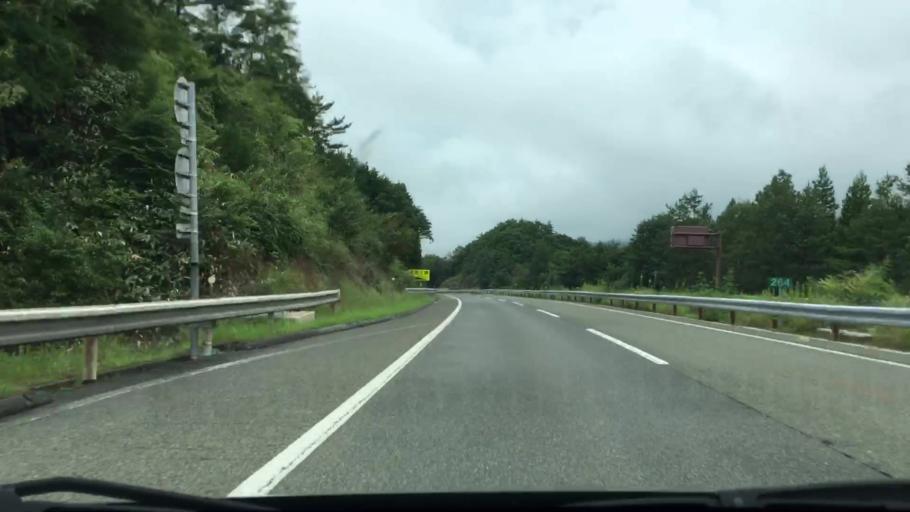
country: JP
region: Hiroshima
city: Shobara
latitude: 34.8747
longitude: 133.1212
